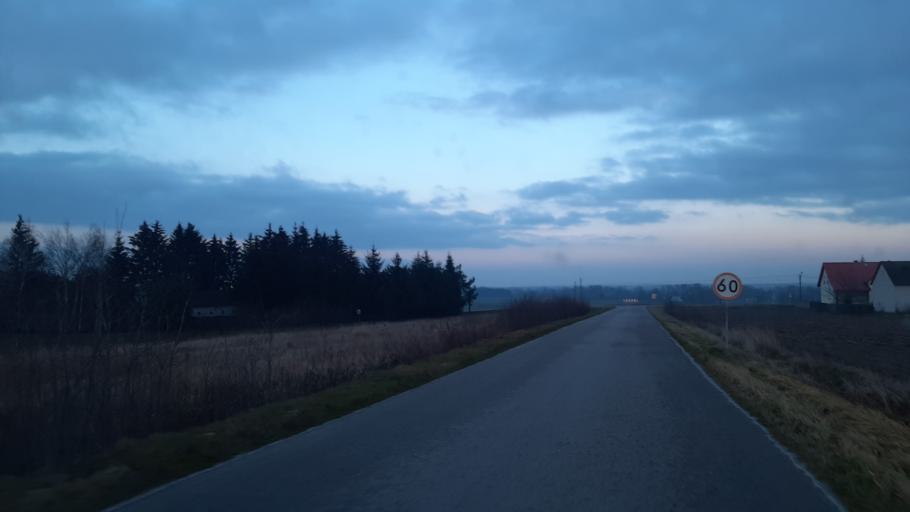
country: PL
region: Lublin Voivodeship
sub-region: Powiat lubartowski
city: Firlej
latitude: 51.5684
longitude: 22.5251
